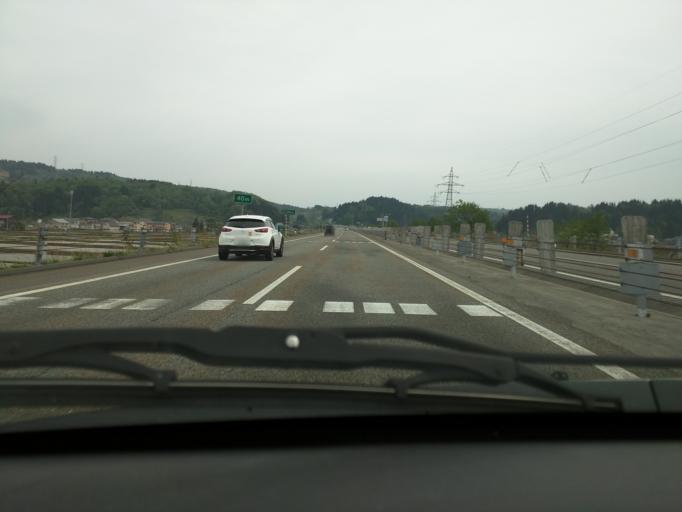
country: JP
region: Niigata
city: Ojiya
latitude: 37.2925
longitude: 138.7831
